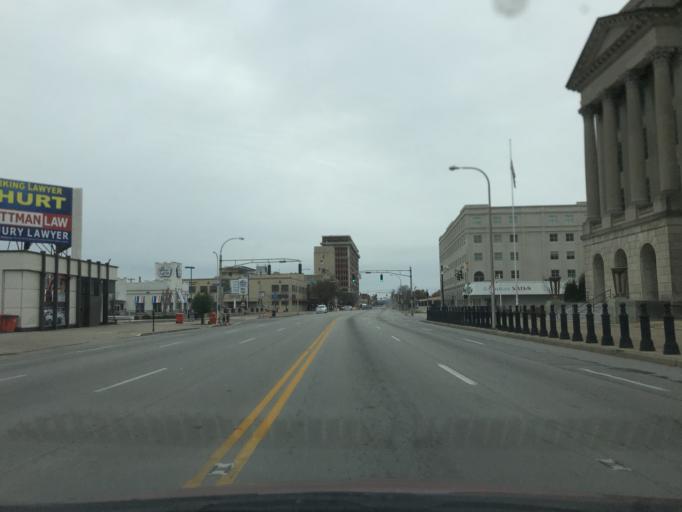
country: US
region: Kentucky
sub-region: Jefferson County
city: Louisville
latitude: 38.2464
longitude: -85.7626
